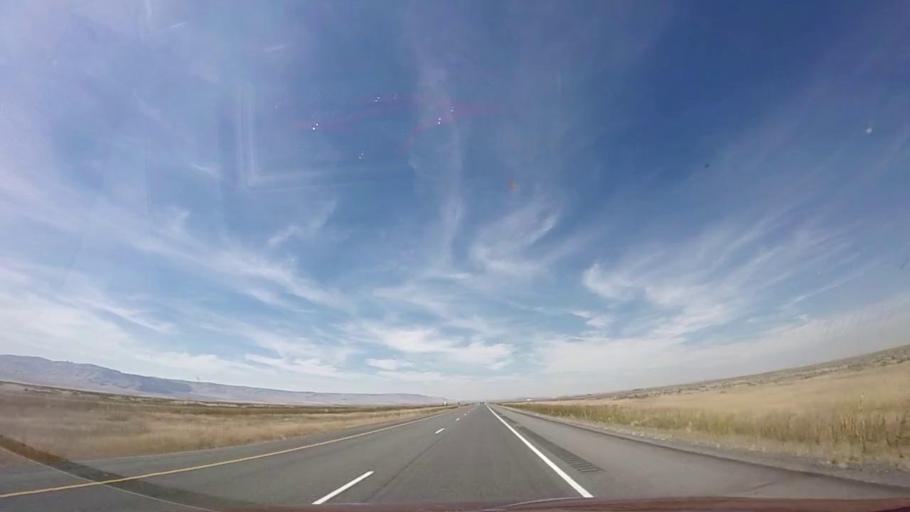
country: US
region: Idaho
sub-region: Minidoka County
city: Rupert
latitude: 42.3649
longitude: -113.2600
